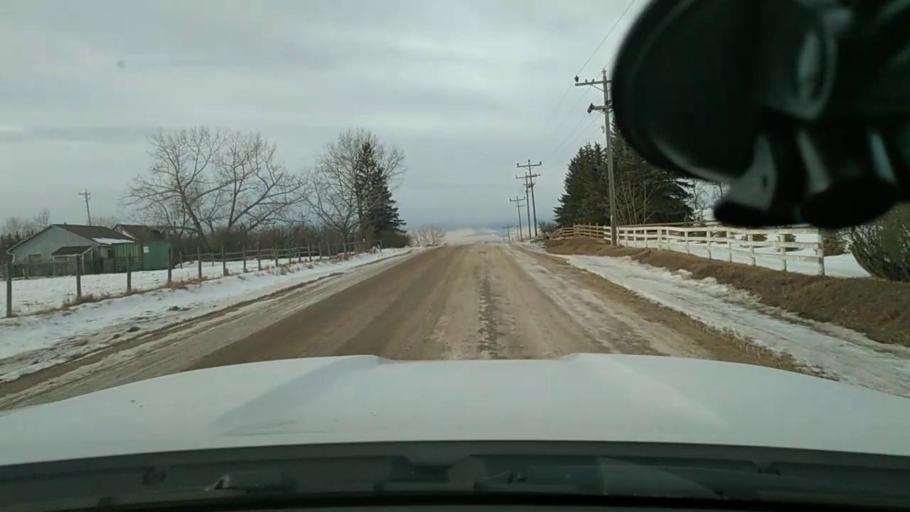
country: CA
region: Alberta
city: Airdrie
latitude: 51.2417
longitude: -113.9334
